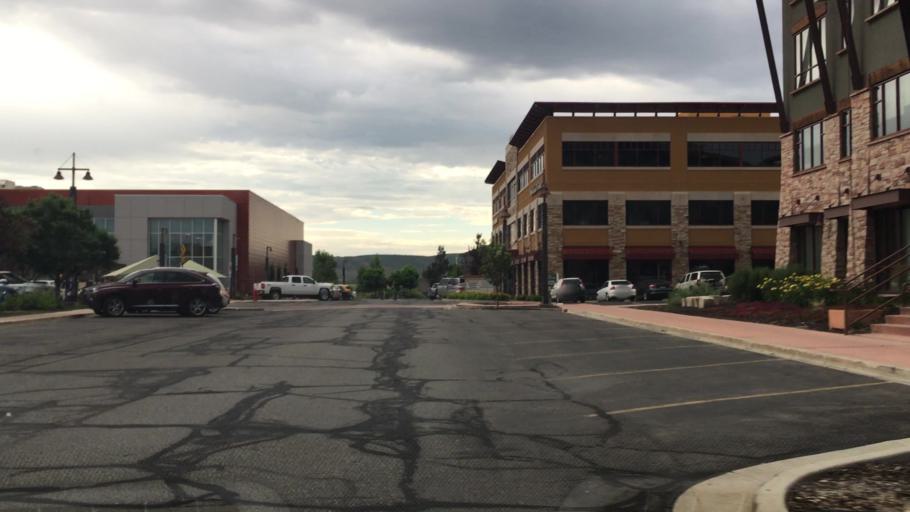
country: US
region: Utah
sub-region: Summit County
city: Snyderville
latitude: 40.7240
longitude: -111.5386
